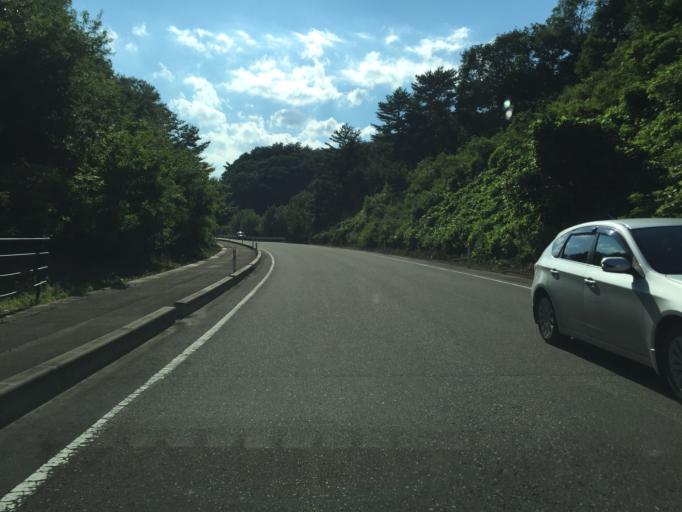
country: JP
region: Fukushima
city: Hobaramachi
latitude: 37.9362
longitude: 140.3964
